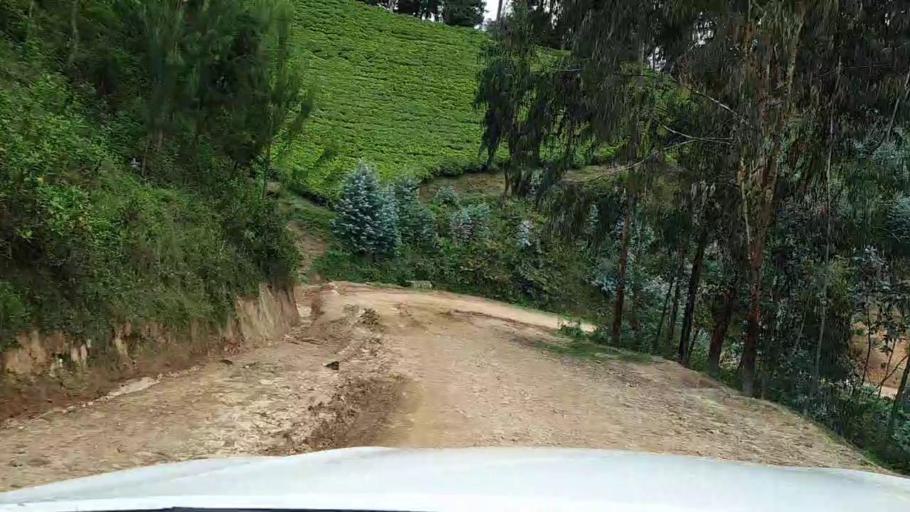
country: RW
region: Western Province
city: Kibuye
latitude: -2.2896
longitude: 29.3730
